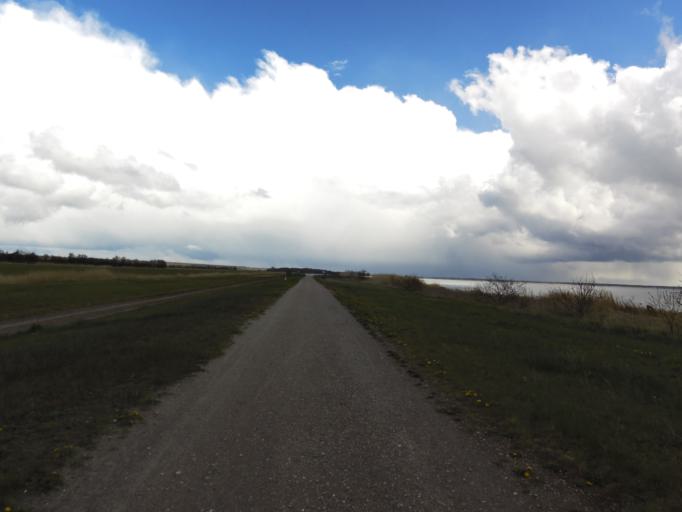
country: DE
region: Mecklenburg-Vorpommern
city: Born
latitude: 54.3819
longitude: 12.4665
